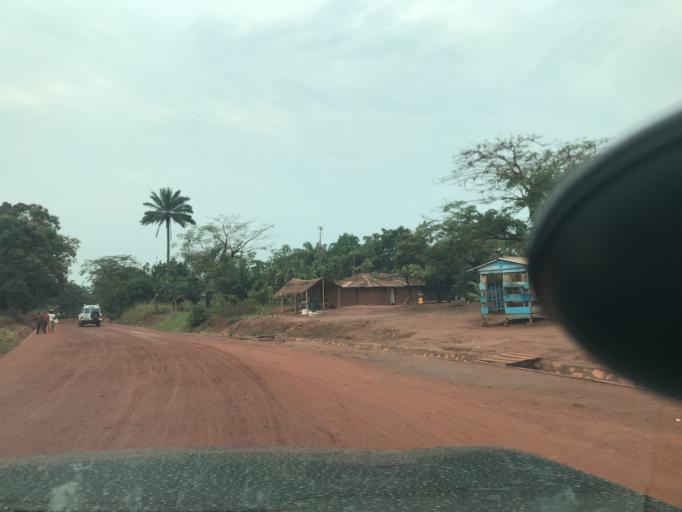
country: CD
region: Equateur
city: Gemena
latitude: 3.2312
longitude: 19.7783
